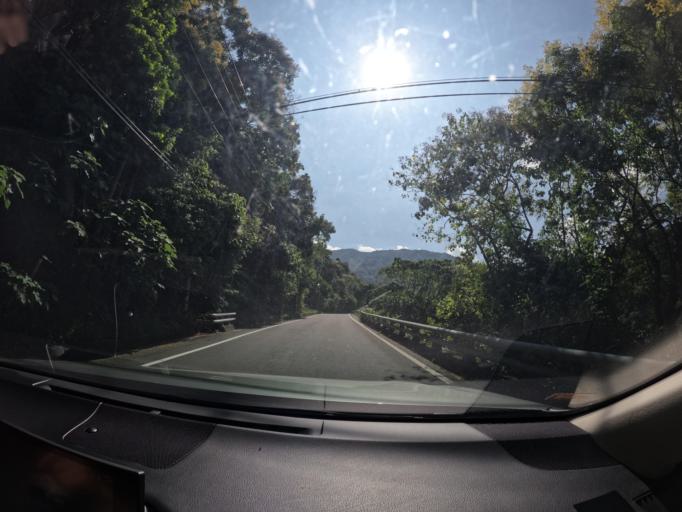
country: TW
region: Taiwan
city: Yujing
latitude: 23.1110
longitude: 120.7074
